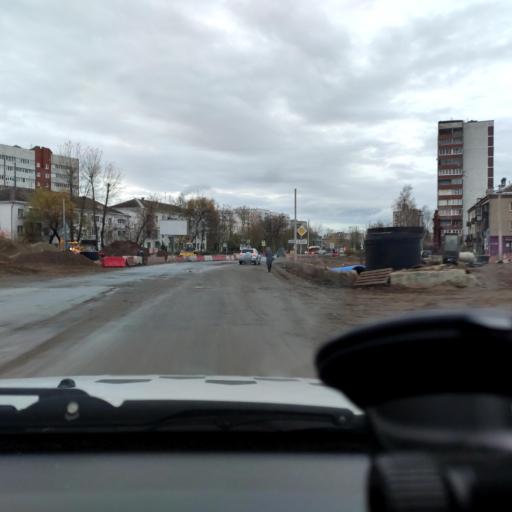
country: RU
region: Perm
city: Perm
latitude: 57.9735
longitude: 56.2077
